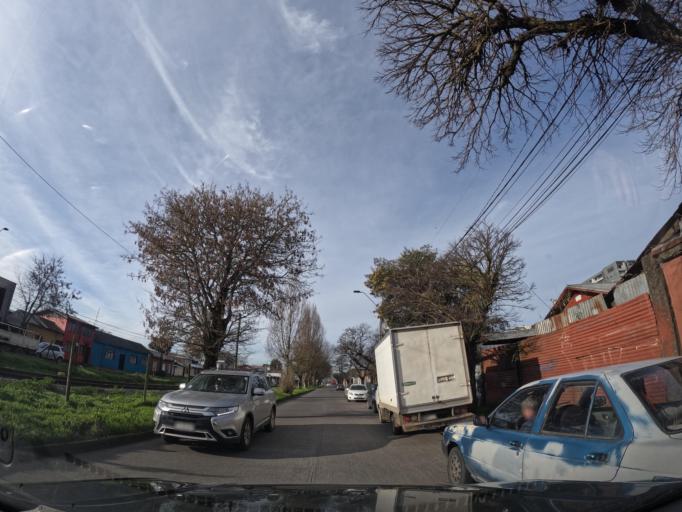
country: CL
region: Biobio
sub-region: Provincia de Concepcion
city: Concepcion
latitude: -36.8137
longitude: -73.0527
